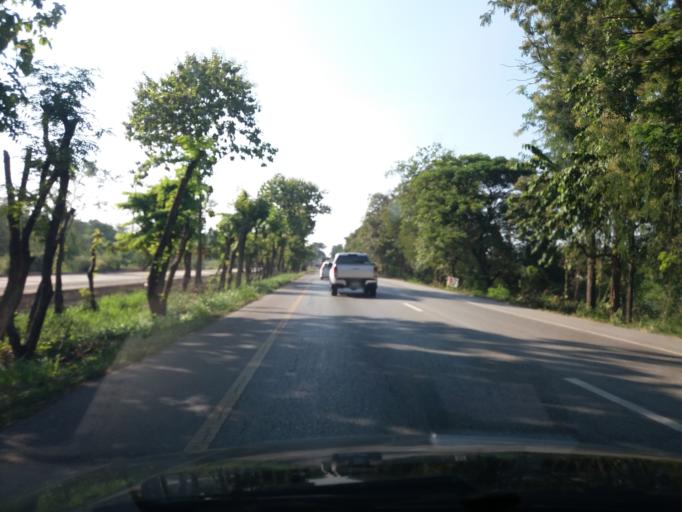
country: TH
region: Nakhon Sawan
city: Nakhon Sawan
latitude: 15.7386
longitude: 100.0189
